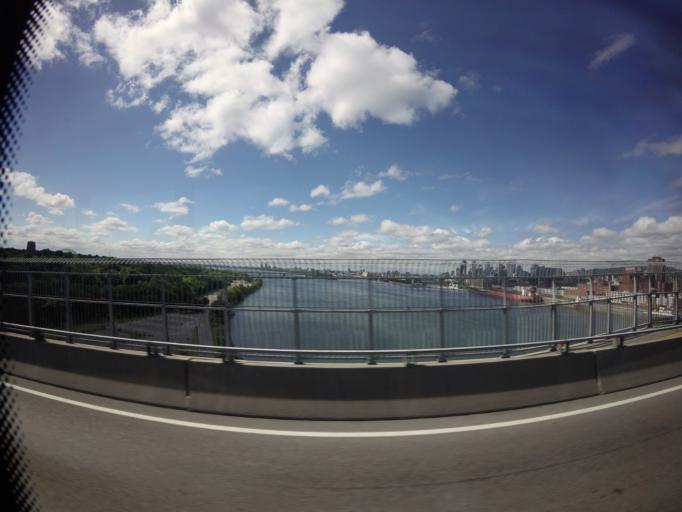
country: CA
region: Quebec
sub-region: Monteregie
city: Longueuil
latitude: 45.5212
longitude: -73.5387
